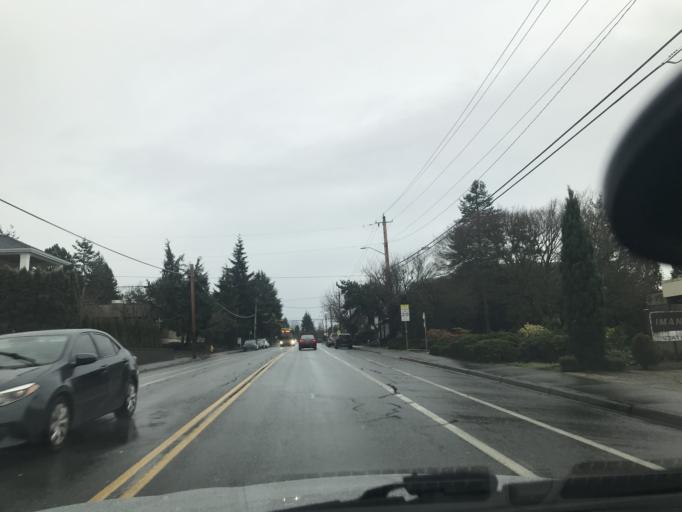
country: US
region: Washington
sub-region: King County
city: Kirkland
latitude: 47.6717
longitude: -122.2023
